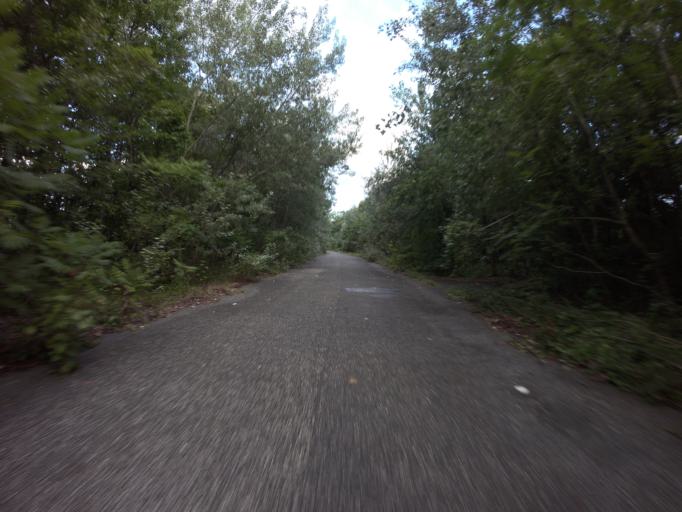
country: US
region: Maryland
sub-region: Baltimore County
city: Edgemere
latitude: 39.2338
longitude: -76.4497
